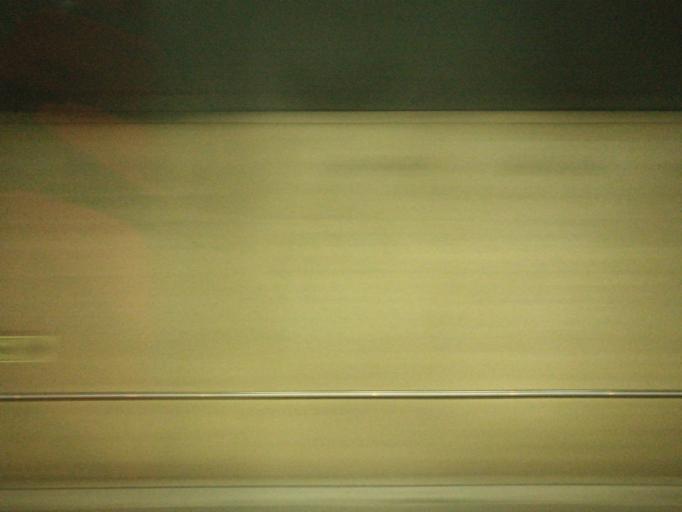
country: NO
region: Oslo
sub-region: Oslo
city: Oslo
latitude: 59.9026
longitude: 10.7744
